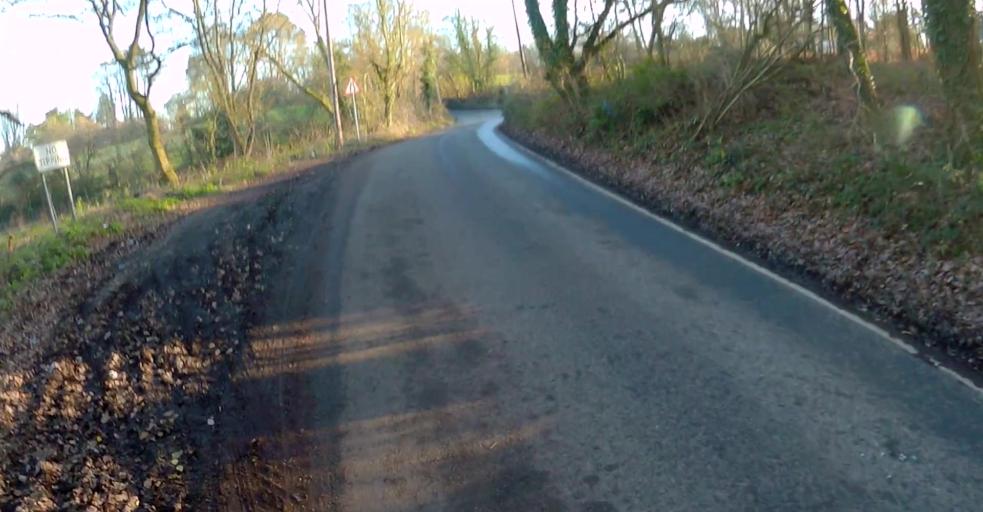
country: GB
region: England
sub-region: Hampshire
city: Hook
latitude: 51.2827
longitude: -0.9933
